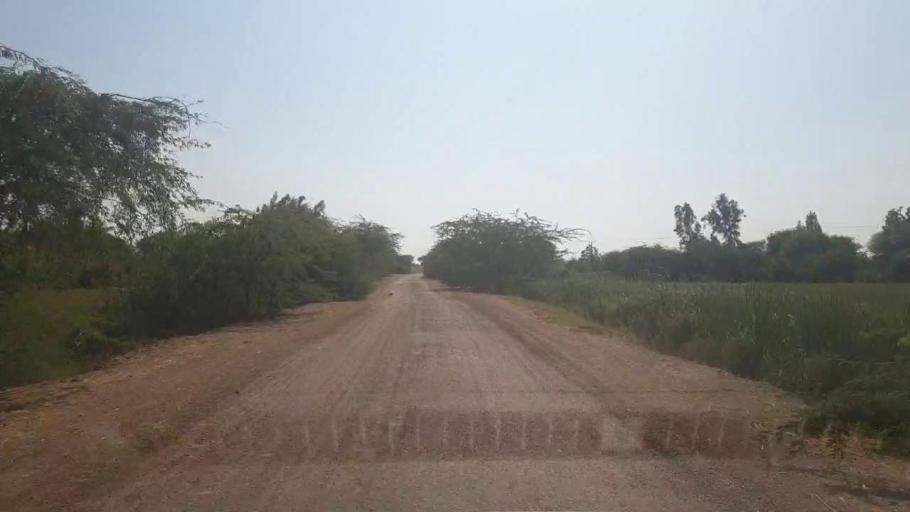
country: PK
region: Sindh
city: Badin
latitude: 24.5793
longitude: 68.8459
